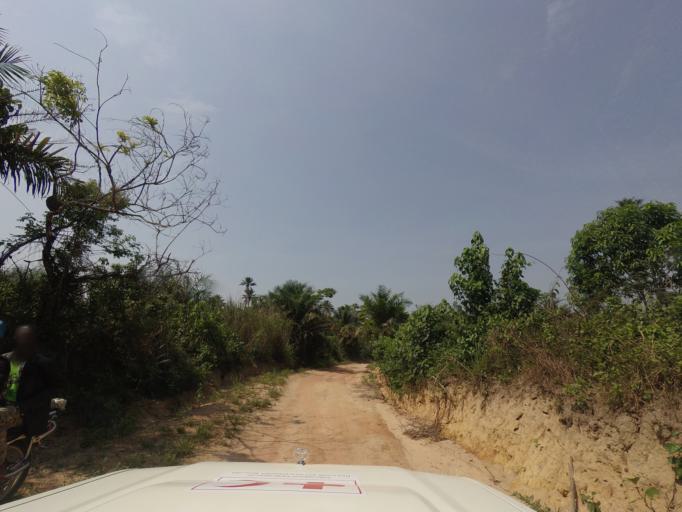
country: LR
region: Lofa
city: Voinjama
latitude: 8.5076
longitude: -9.6343
